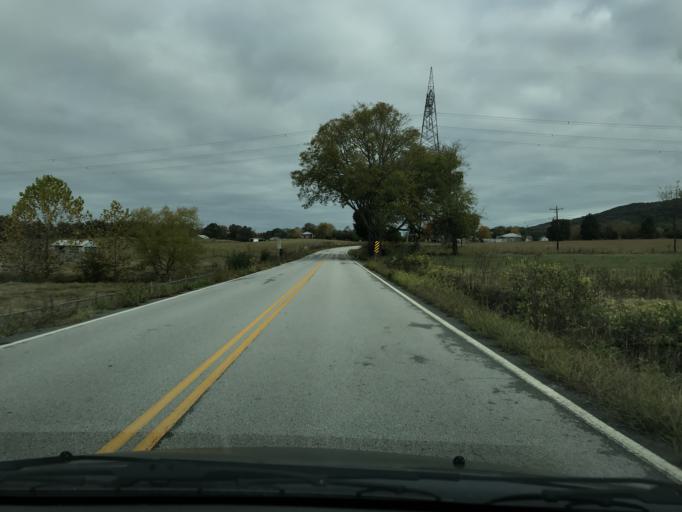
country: US
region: Tennessee
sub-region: Hamilton County
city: Lakesite
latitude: 35.1810
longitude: -85.0253
